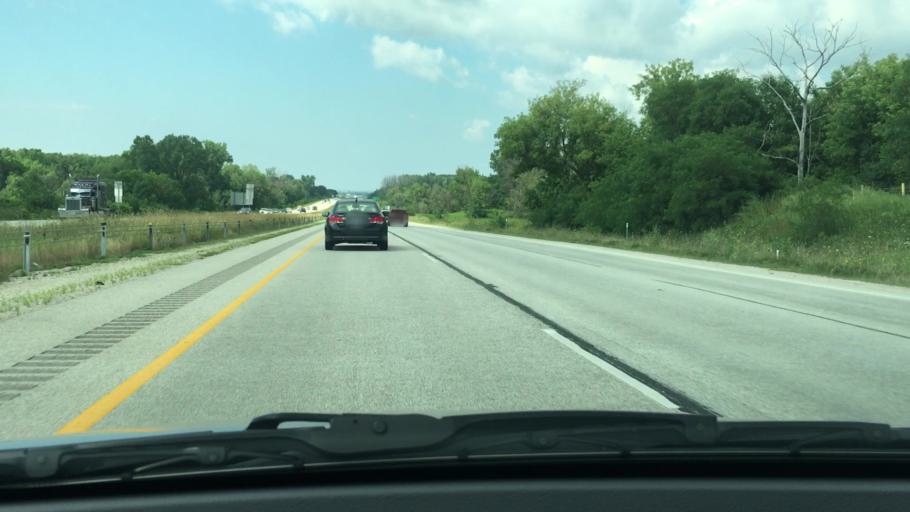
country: US
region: Wisconsin
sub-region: Fond du Lac County
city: Fond du Lac
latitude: 43.6969
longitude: -88.4420
